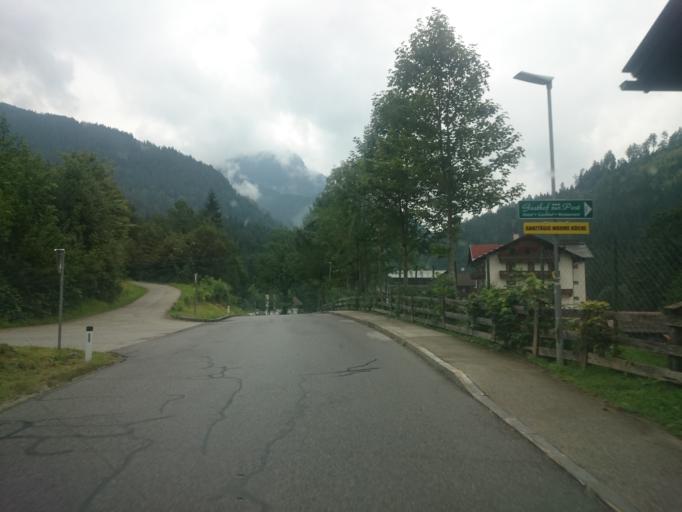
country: DE
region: Bavaria
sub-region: Upper Bavaria
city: Jachenau
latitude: 47.4720
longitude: 11.4677
